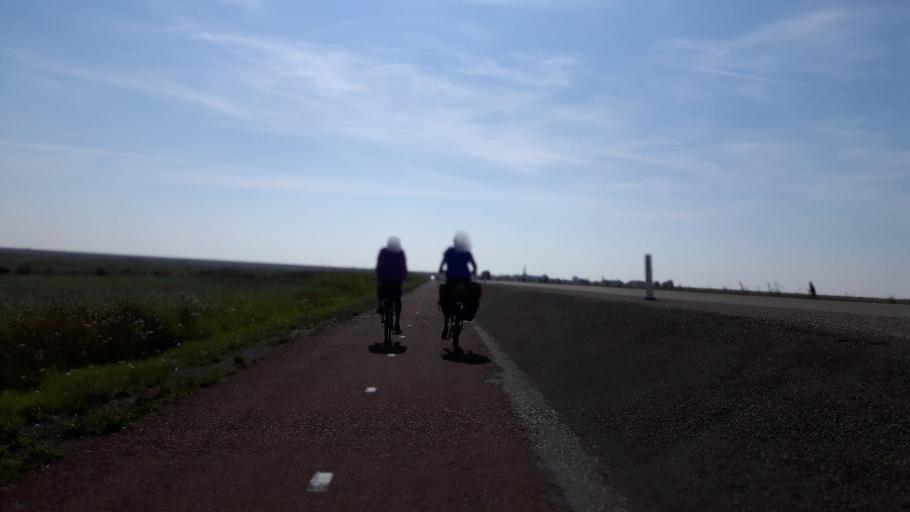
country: NL
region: Friesland
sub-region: Gemeente Dongeradeel
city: Holwerd
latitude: 53.3870
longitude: 5.8874
